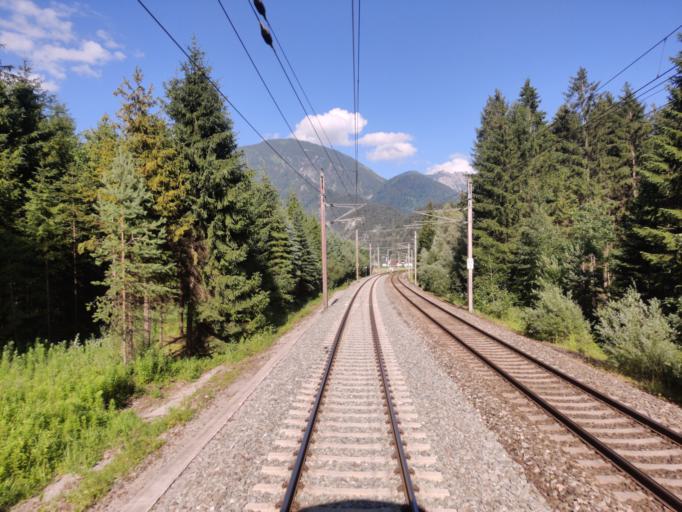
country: AT
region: Vorarlberg
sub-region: Politischer Bezirk Bludenz
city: Thuringen
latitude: 47.1817
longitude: 9.7603
